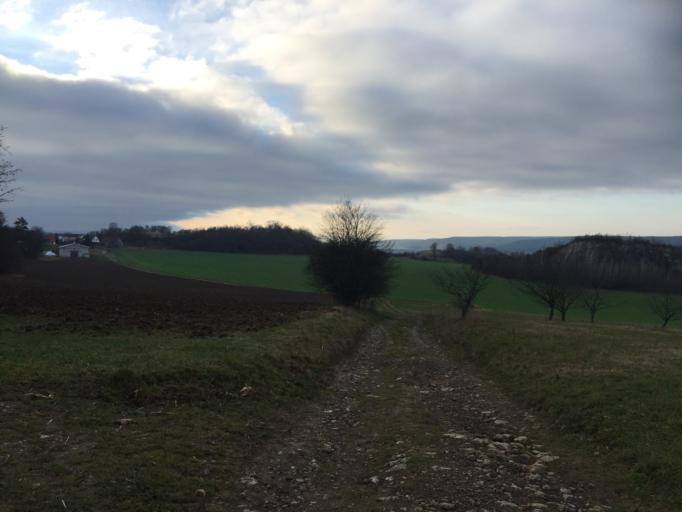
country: DE
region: Thuringia
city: Ranis
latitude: 50.6744
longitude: 11.5656
